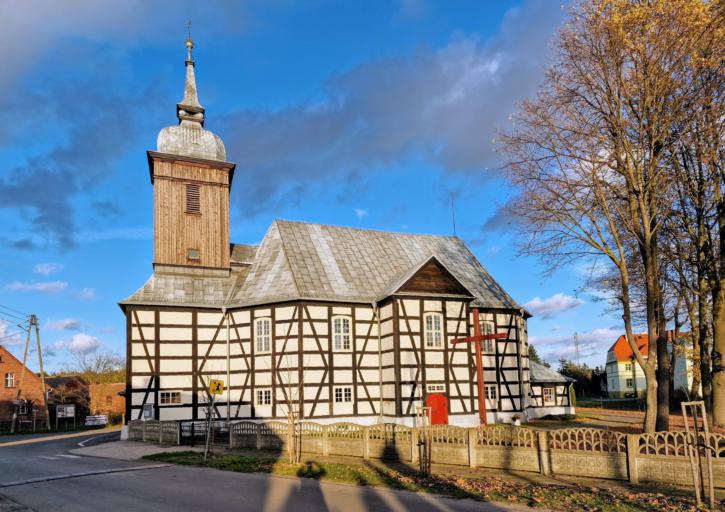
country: PL
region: Lubusz
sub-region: Powiat zielonogorski
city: Bojadla
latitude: 51.9532
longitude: 15.8122
